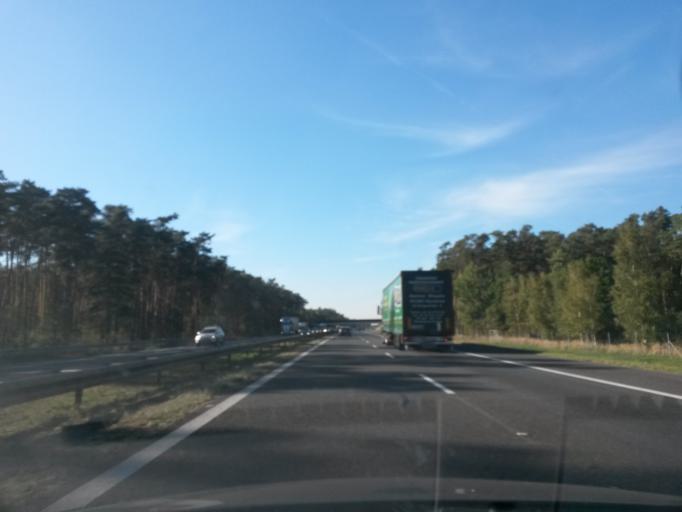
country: PL
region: Opole Voivodeship
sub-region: Powiat opolski
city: Niemodlin
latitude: 50.6691
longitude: 17.6727
